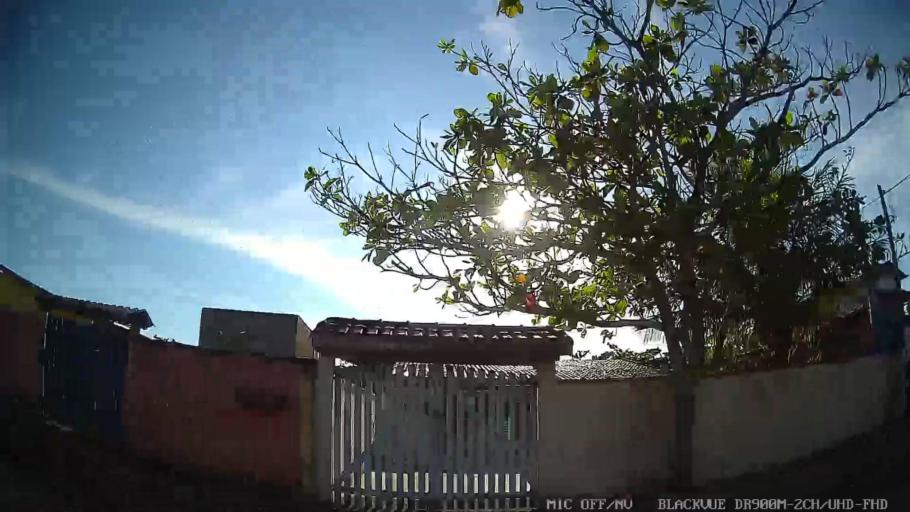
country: BR
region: Sao Paulo
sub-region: Iguape
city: Iguape
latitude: -24.7584
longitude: -47.5737
